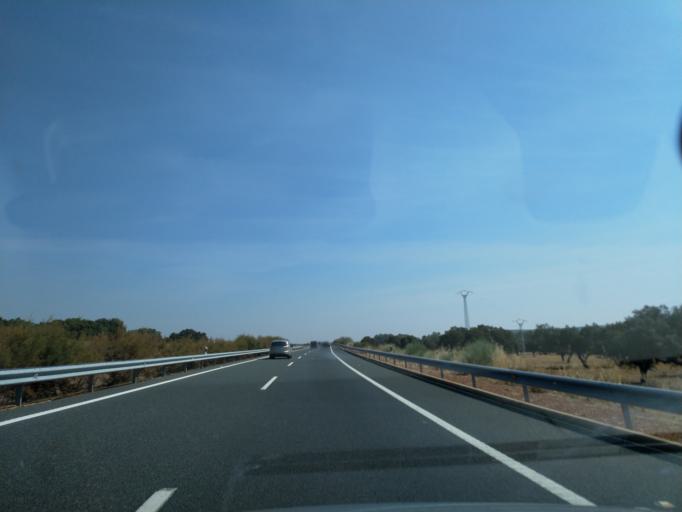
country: ES
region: Extremadura
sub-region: Provincia de Badajoz
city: Aljucen
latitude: 39.0523
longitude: -6.3315
